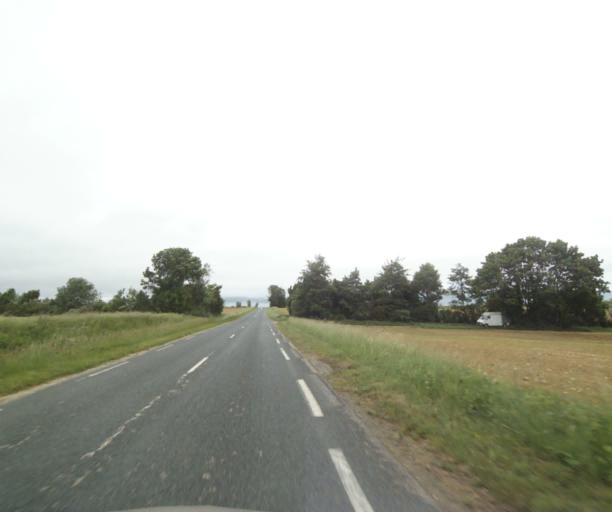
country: FR
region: Rhone-Alpes
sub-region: Departement de l'Ain
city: Mionnay
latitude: 45.8613
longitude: 4.9229
